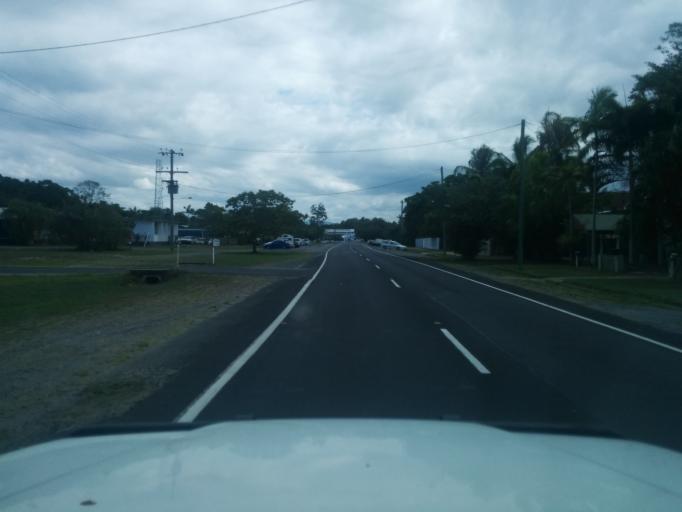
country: AU
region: Queensland
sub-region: Cairns
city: Cairns
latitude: -16.9103
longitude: 145.7502
